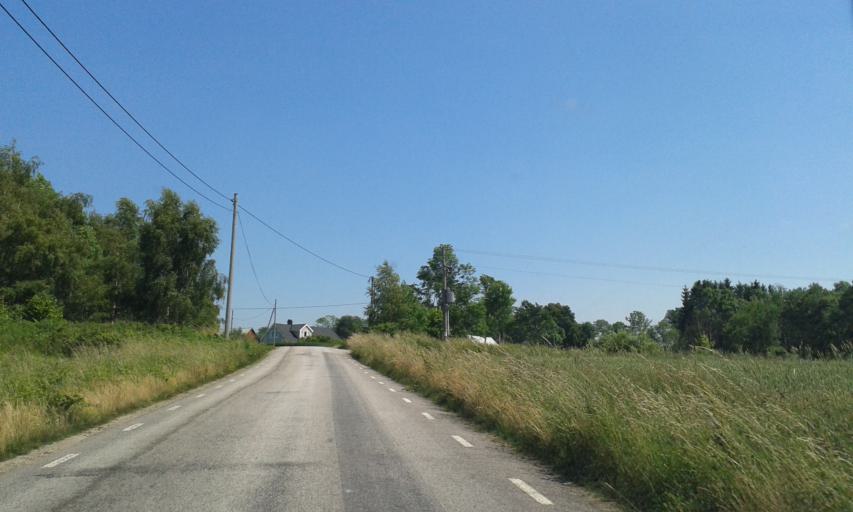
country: SE
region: Blekinge
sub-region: Karlskrona Kommun
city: Rodeby
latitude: 56.2580
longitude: 15.5491
